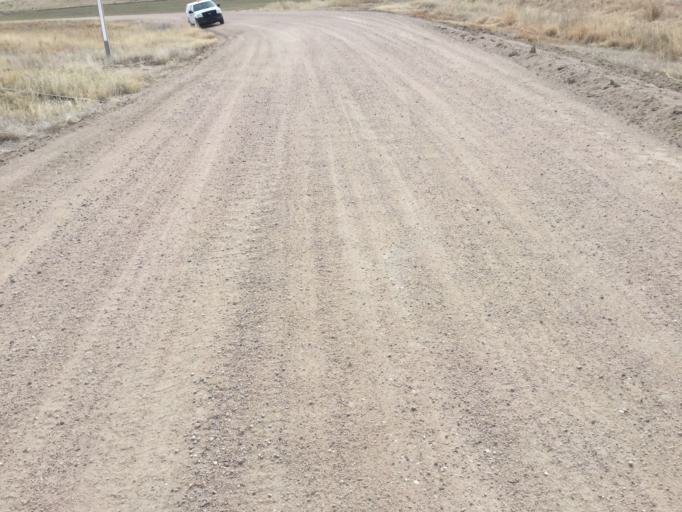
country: US
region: Kansas
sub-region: Rawlins County
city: Atwood
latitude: 39.8577
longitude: -100.9246
